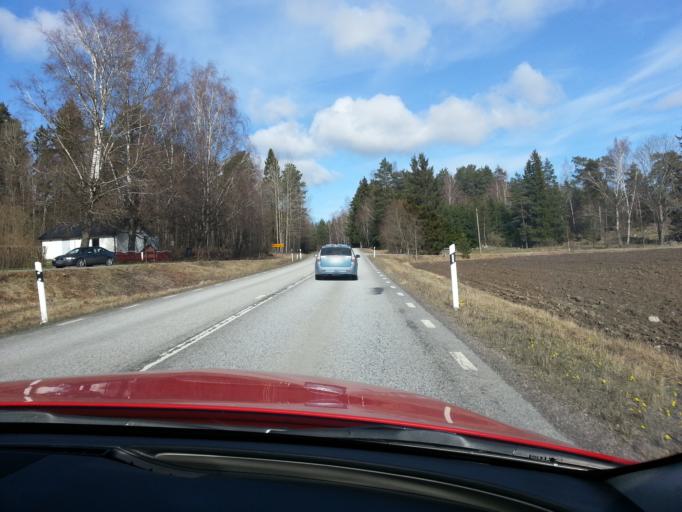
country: SE
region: Uppsala
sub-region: Osthammars Kommun
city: Gimo
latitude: 60.0956
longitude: 18.1241
